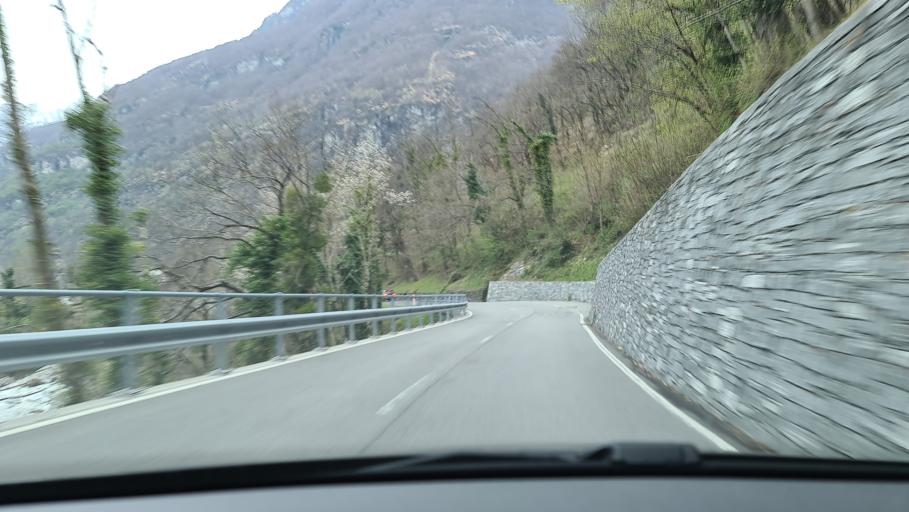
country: CH
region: Ticino
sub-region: Vallemaggia District
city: Cevio
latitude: 46.3481
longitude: 8.6139
